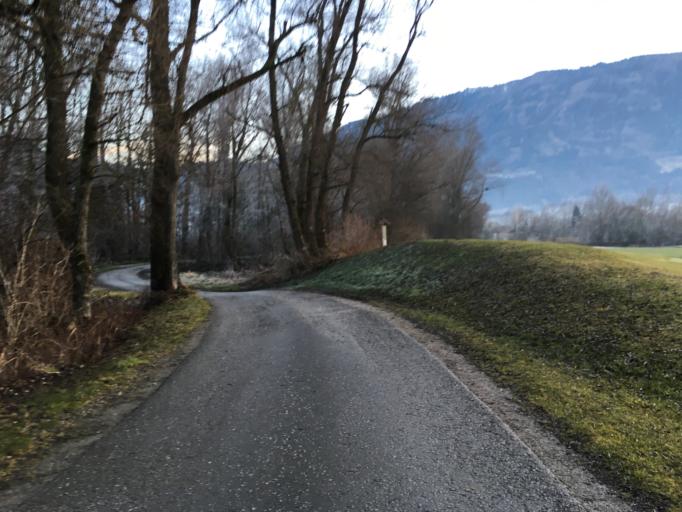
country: AT
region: Styria
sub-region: Politischer Bezirk Liezen
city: Weissenbach bei Liezen
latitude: 47.5568
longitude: 14.2020
